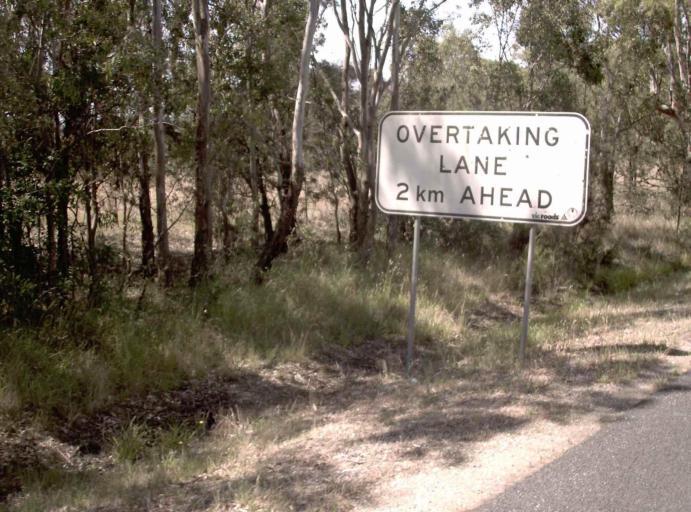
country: AU
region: Victoria
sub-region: Wellington
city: Sale
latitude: -37.9549
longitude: 147.1024
